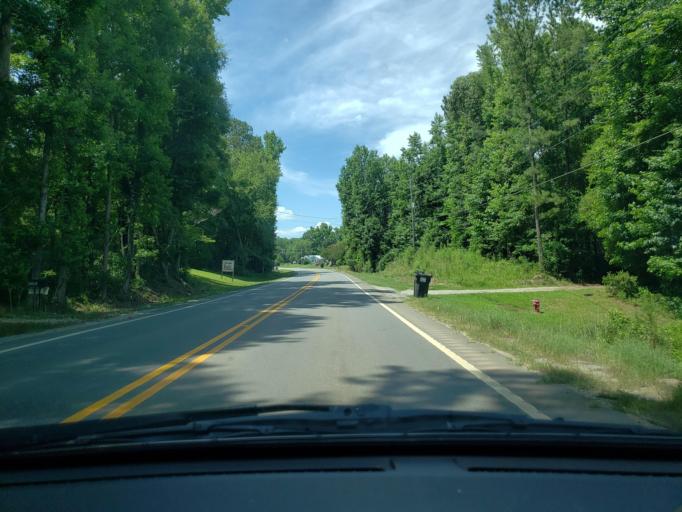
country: US
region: Alabama
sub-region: Elmore County
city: Eclectic
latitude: 32.6679
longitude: -85.9424
